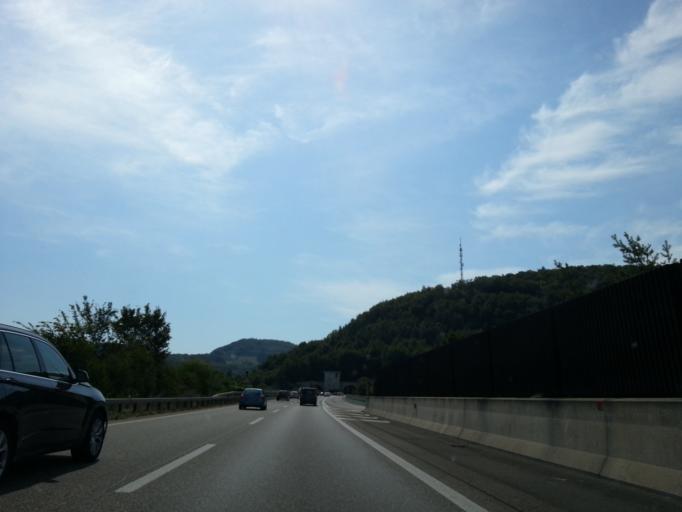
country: CH
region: Basel-Landschaft
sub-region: Bezirk Sissach
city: Sissach
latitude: 47.4669
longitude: 7.7980
